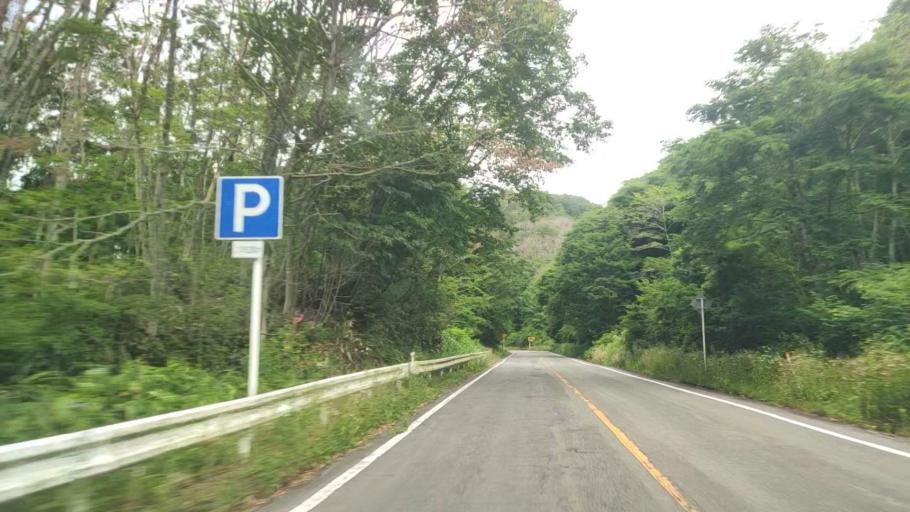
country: JP
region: Tottori
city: Kurayoshi
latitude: 35.3277
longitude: 133.5942
